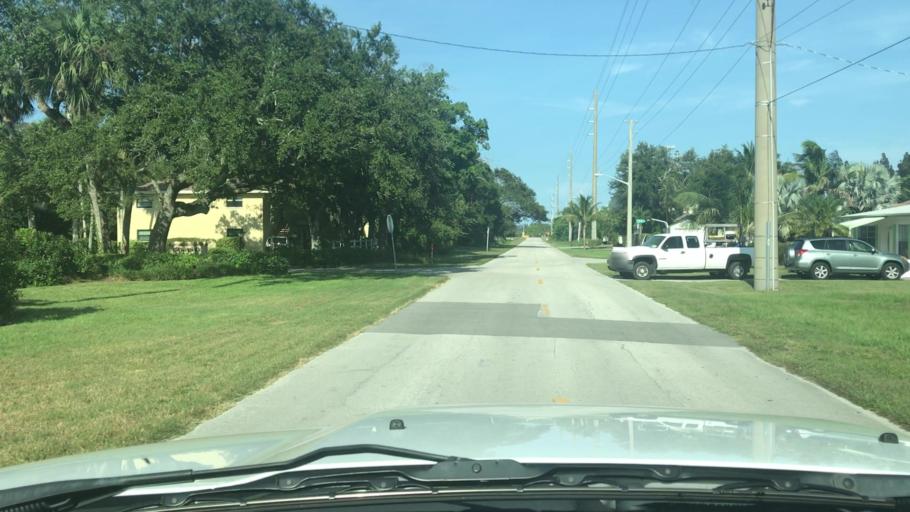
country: US
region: Florida
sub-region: Indian River County
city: Vero Beach
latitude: 27.6343
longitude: -80.3841
